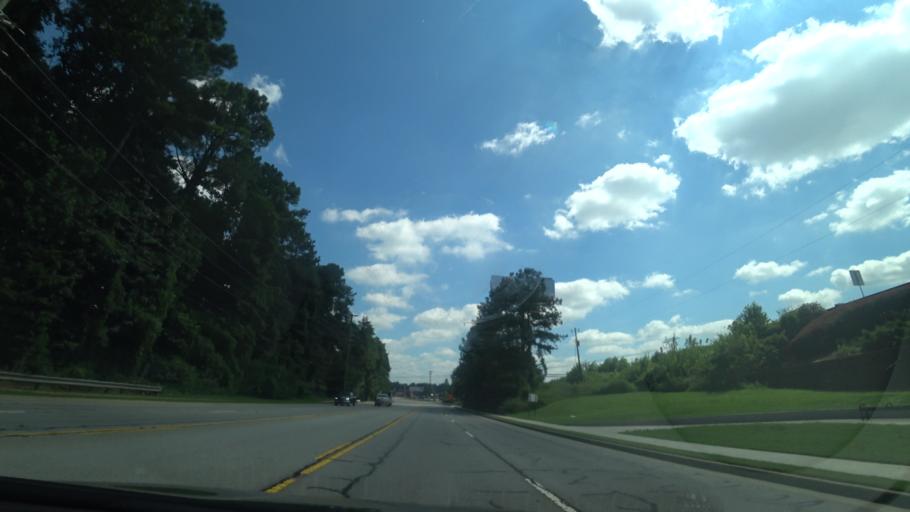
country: US
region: Georgia
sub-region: Gwinnett County
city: Norcross
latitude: 33.9232
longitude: -84.1884
